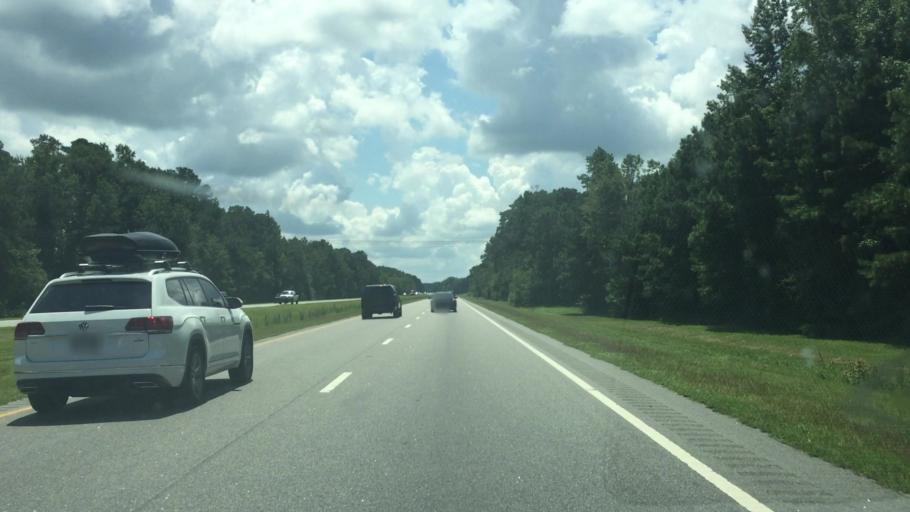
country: US
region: North Carolina
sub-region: Robeson County
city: Lumberton
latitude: 34.5397
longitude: -79.0200
